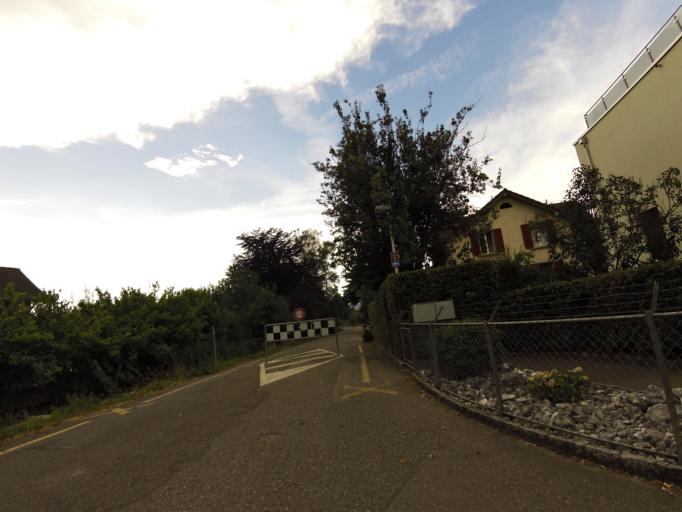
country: CH
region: Aargau
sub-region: Bezirk Aarau
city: Suhr
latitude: 47.3817
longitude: 8.0681
